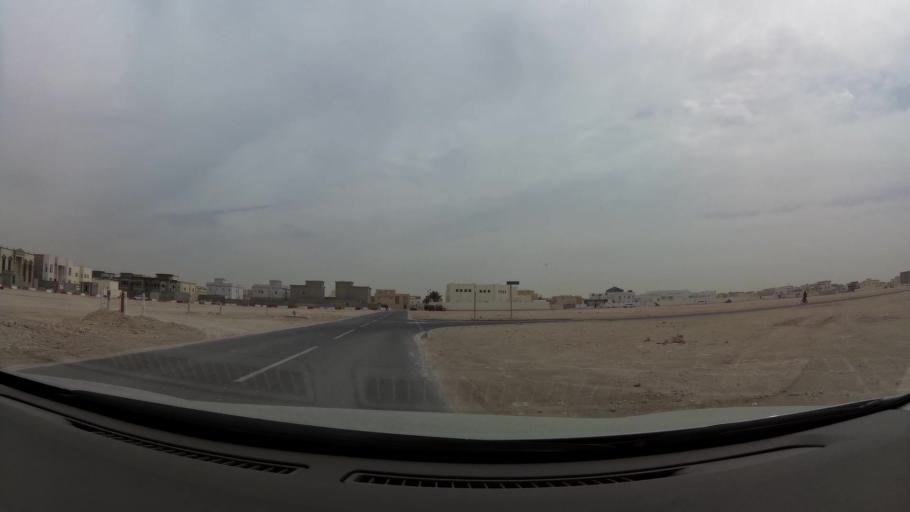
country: QA
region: Baladiyat ar Rayyan
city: Ar Rayyan
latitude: 25.2138
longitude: 51.4629
